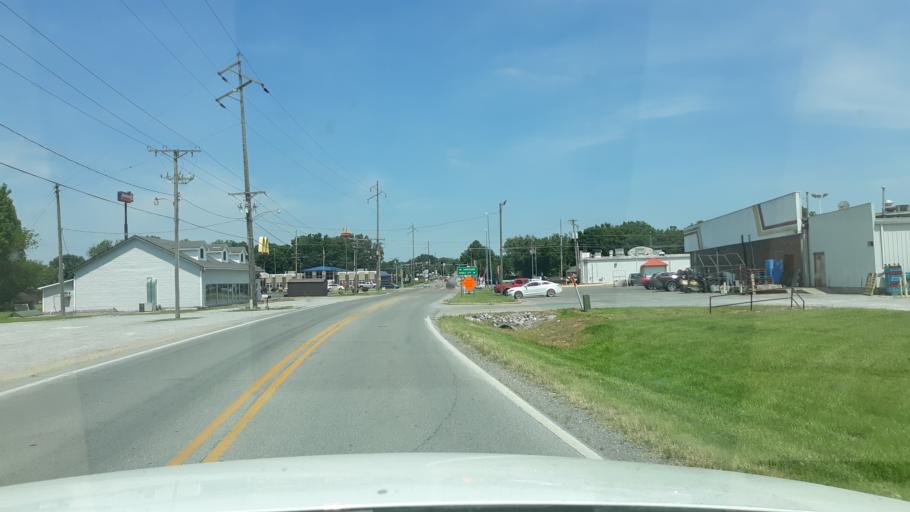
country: US
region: Illinois
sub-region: Saline County
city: Eldorado
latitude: 37.8056
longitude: -88.4389
